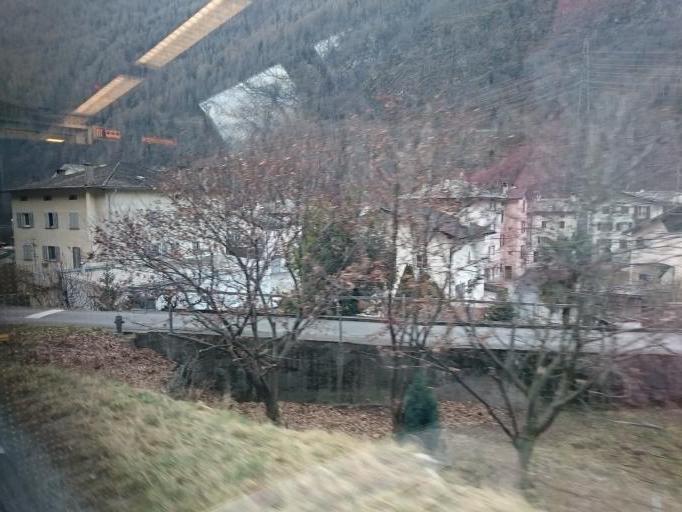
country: CH
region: Grisons
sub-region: Bernina District
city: Brusio
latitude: 46.2457
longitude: 10.1318
